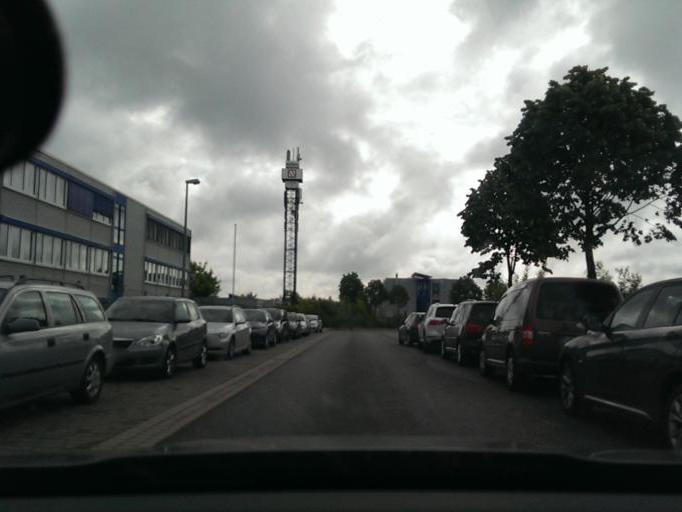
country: DE
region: Lower Saxony
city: Wolfsburg
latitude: 52.3726
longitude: 10.7407
